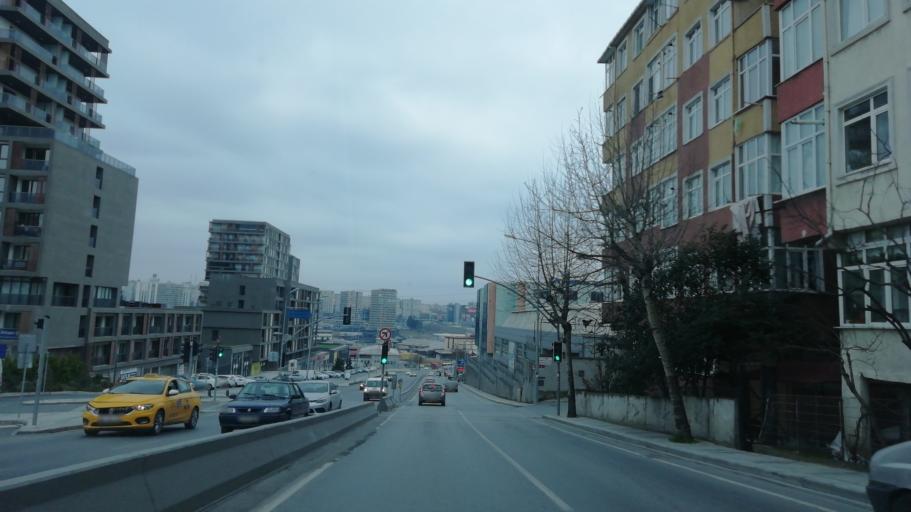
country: TR
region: Istanbul
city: Mahmutbey
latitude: 41.0088
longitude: 28.8039
